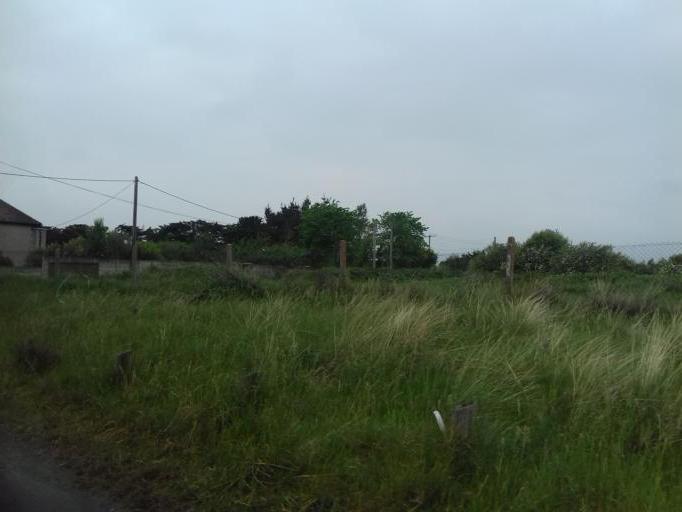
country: IE
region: Leinster
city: Portraine
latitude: 53.4747
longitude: -6.1234
